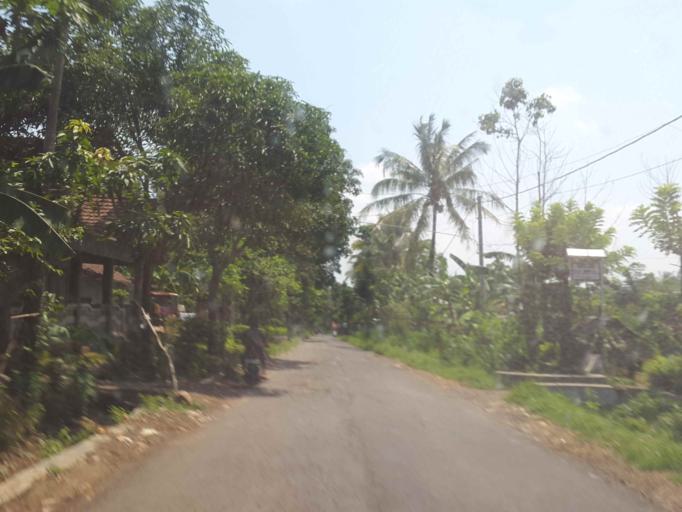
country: ID
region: East Java
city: Krajan Satu Pekauman
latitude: -7.9878
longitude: 113.7965
